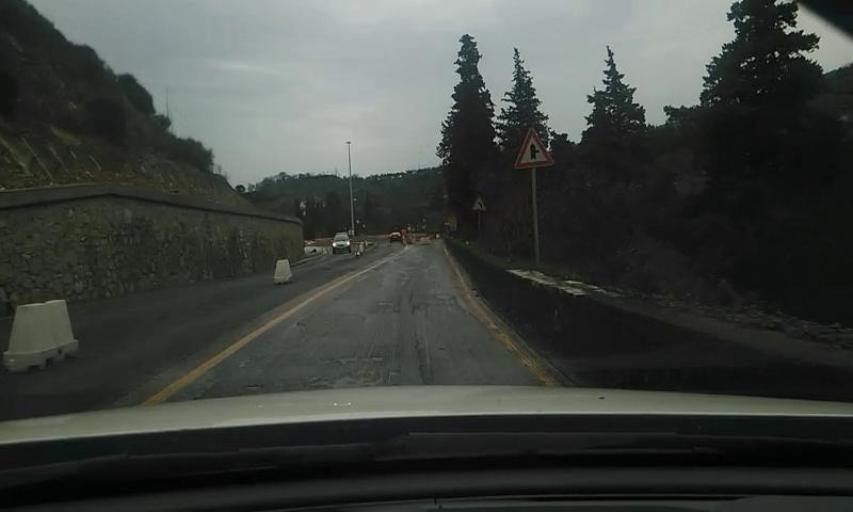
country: IT
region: Tuscany
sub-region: Provincia di Prato
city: Vaiano
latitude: 43.9250
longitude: 11.1269
